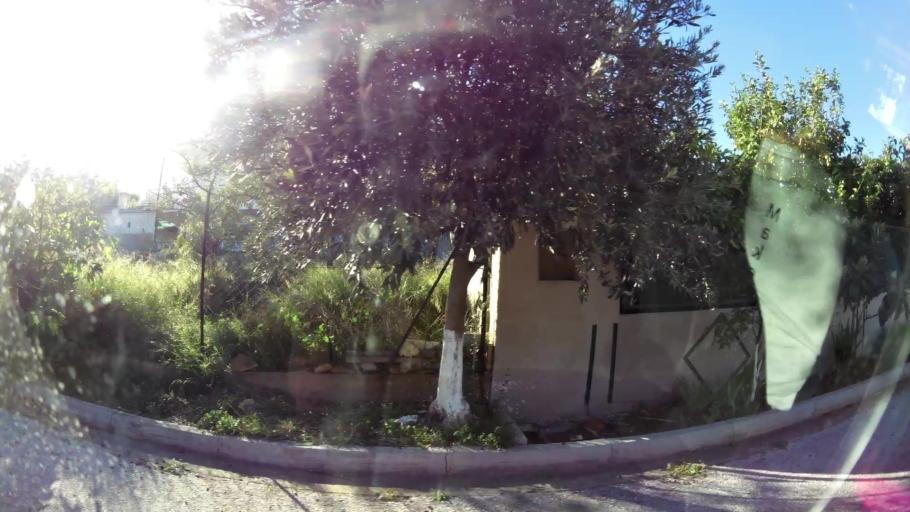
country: GR
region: Attica
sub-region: Nomarchia Anatolikis Attikis
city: Leondarion
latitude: 37.9798
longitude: 23.8435
